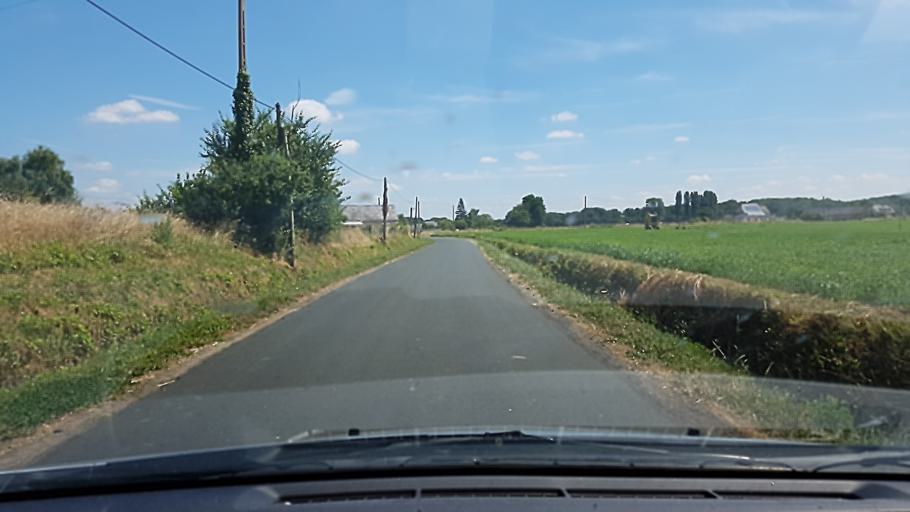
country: FR
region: Pays de la Loire
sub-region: Departement de Maine-et-Loire
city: Corze
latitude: 47.5294
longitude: -0.3990
